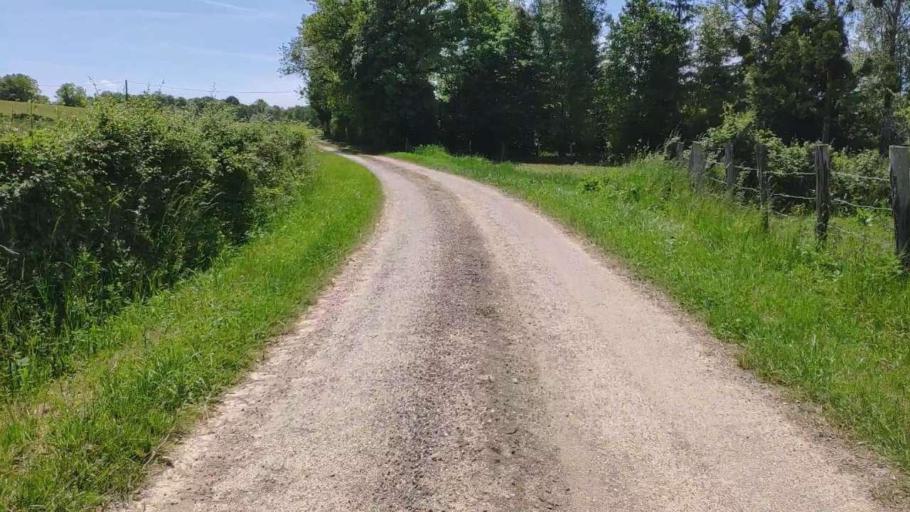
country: FR
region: Franche-Comte
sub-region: Departement du Jura
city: Bletterans
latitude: 46.7896
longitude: 5.3935
